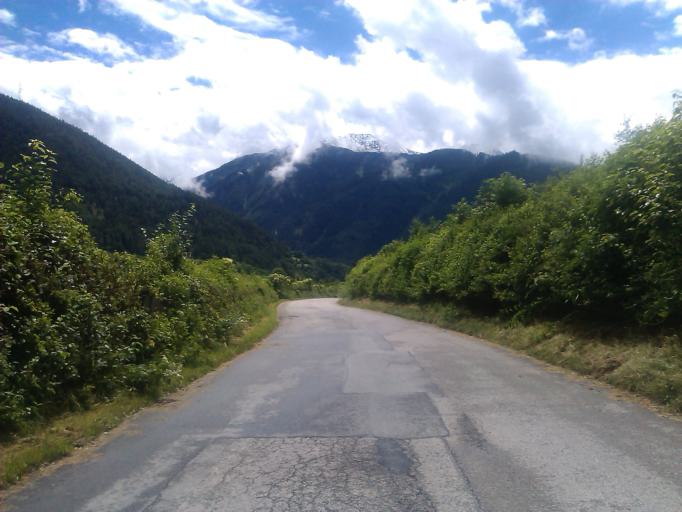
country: AT
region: Tyrol
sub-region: Politischer Bezirk Landeck
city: Prutz
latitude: 47.0922
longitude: 10.6613
